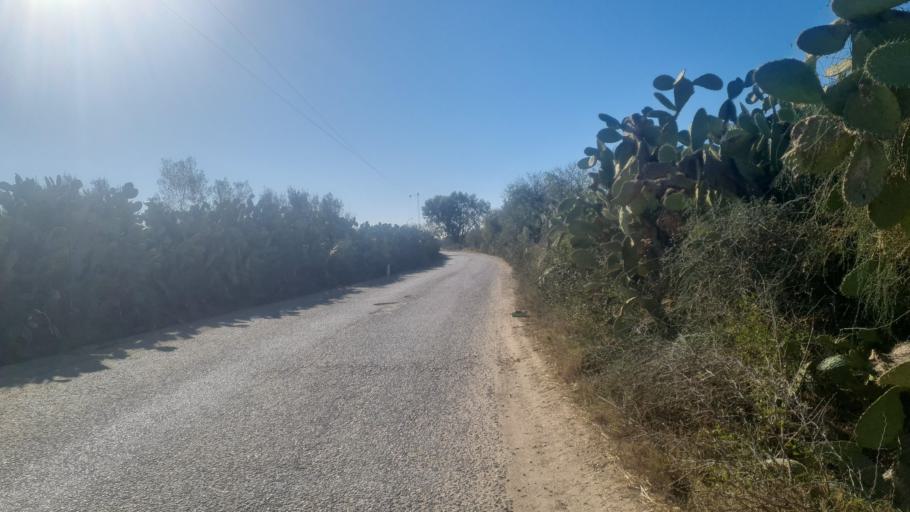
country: TN
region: Susah
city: Sidi Bou Ali
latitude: 35.9081
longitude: 10.3813
